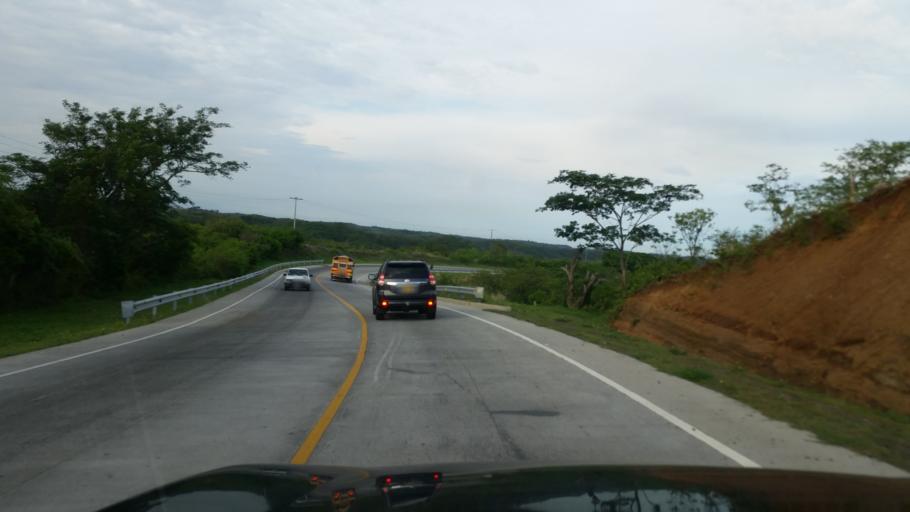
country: NI
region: Managua
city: Ciudad Sandino
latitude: 12.0773
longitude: -86.4263
